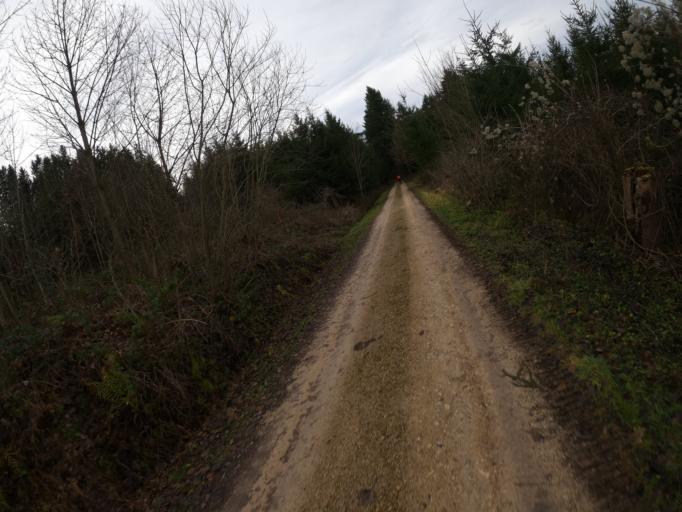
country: DE
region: Baden-Wuerttemberg
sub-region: Regierungsbezirk Stuttgart
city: Ottenbach
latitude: 48.7561
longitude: 9.7644
